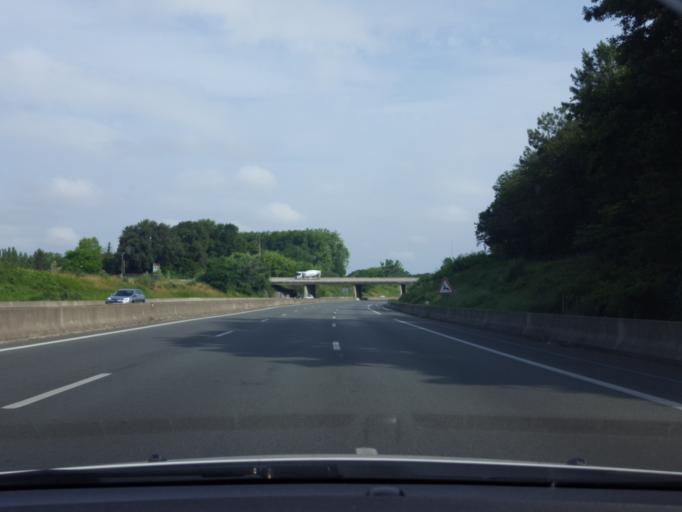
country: FR
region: Aquitaine
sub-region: Departement des Pyrenees-Atlantiques
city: Boucau
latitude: 43.5081
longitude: -1.4418
